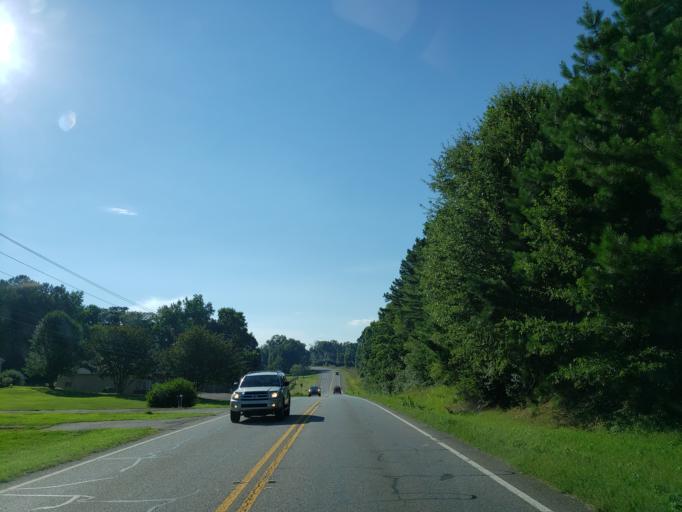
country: US
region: Georgia
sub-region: Cherokee County
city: Ball Ground
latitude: 34.2496
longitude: -84.3089
